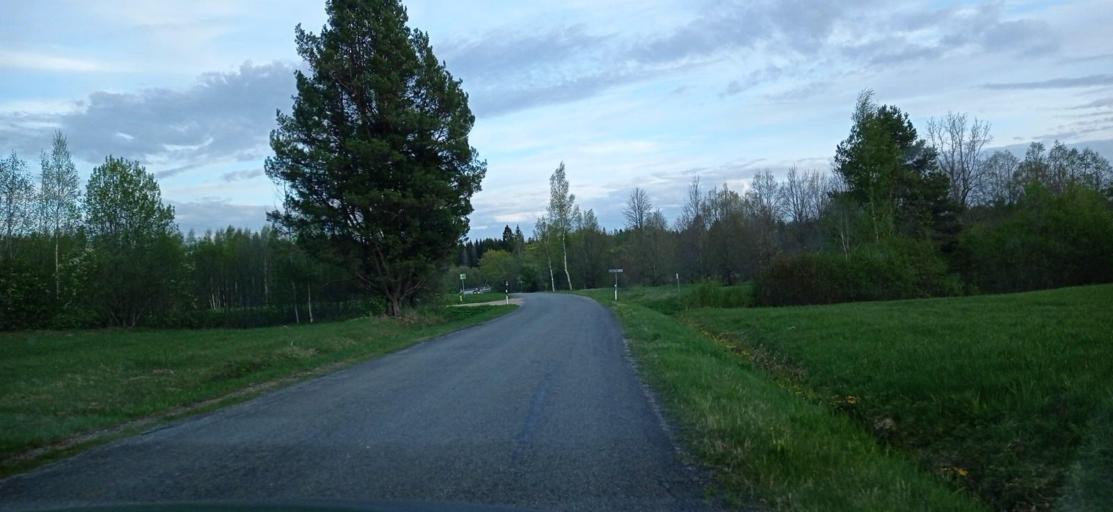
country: EE
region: Jaervamaa
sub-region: Tueri vald
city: Sarevere
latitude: 58.6677
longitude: 25.2546
